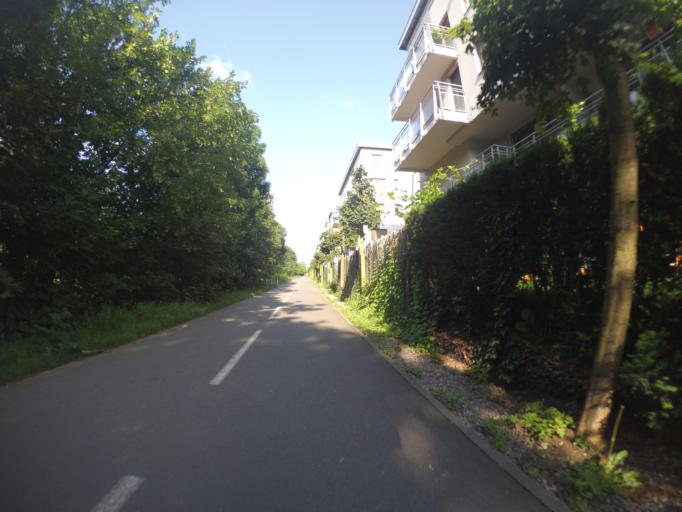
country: CZ
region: Praha
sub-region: Praha 9
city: Vysocany
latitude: 50.1052
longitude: 14.5136
